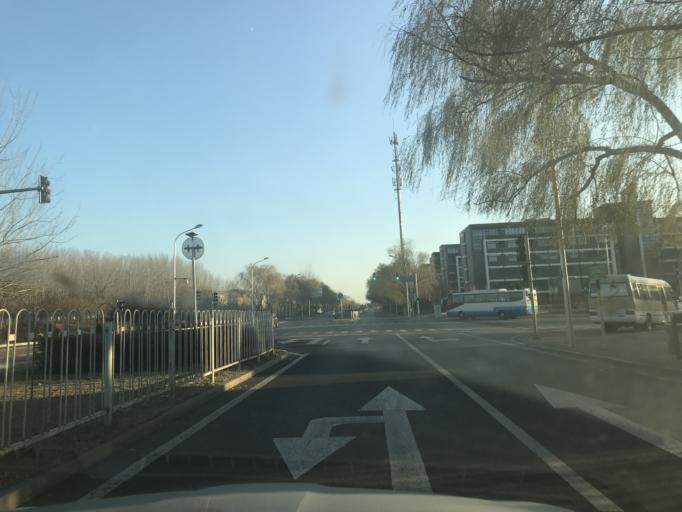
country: CN
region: Beijing
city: Xibeiwang
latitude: 40.0735
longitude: 116.2489
